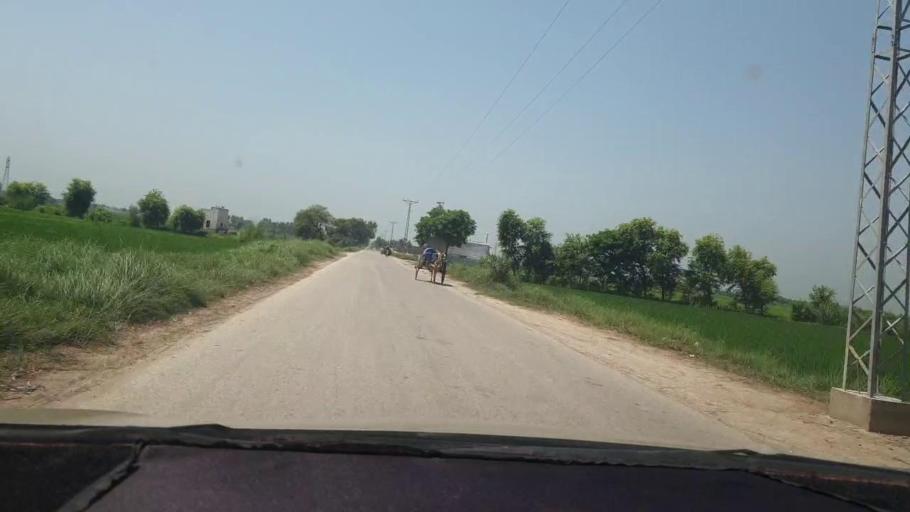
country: PK
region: Sindh
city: Kambar
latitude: 27.6022
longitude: 68.0315
